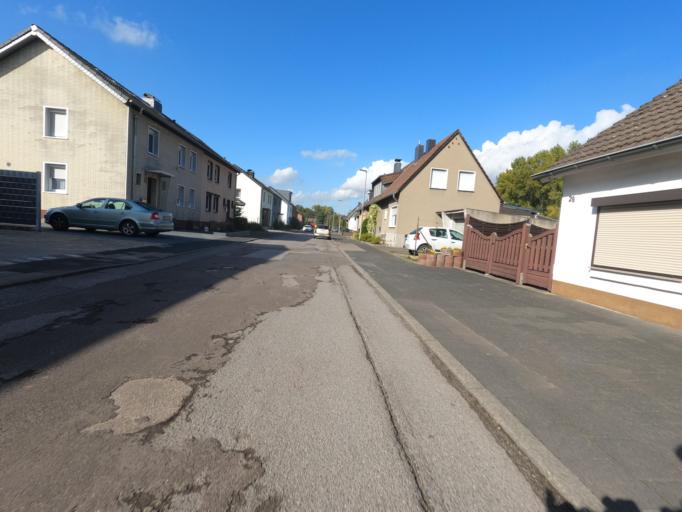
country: DE
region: North Rhine-Westphalia
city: Julich
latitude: 50.8992
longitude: 6.3593
